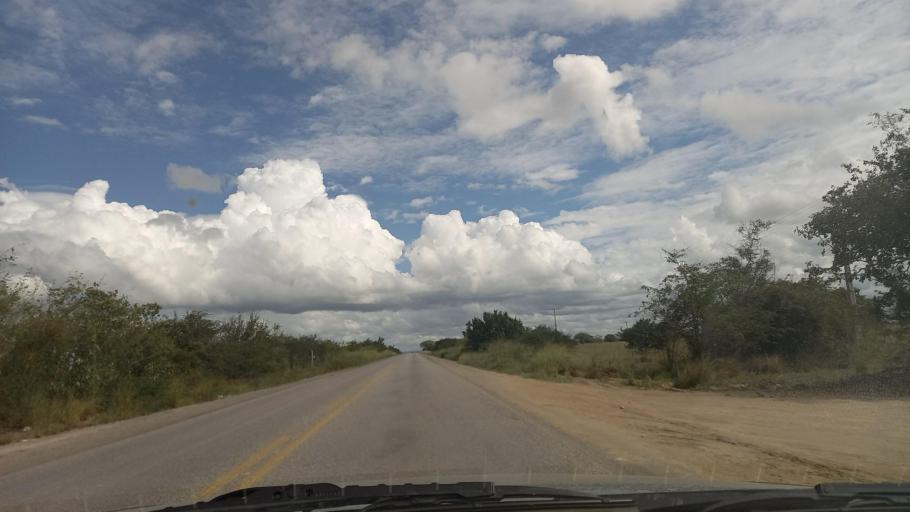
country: BR
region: Pernambuco
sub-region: Cachoeirinha
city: Cachoeirinha
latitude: -8.4411
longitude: -36.2059
